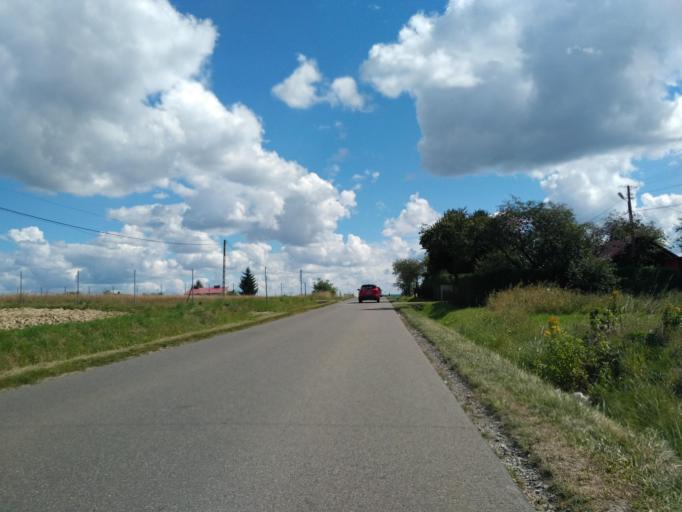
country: PL
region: Subcarpathian Voivodeship
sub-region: Powiat jasielski
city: Trzcinica
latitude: 49.7512
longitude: 21.4281
